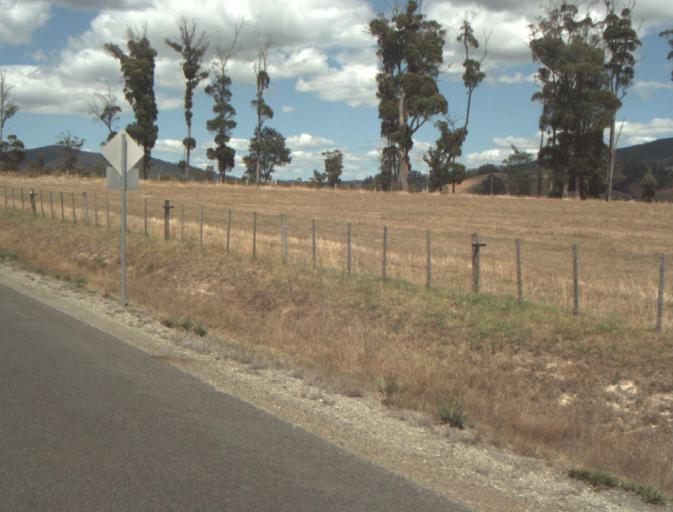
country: AU
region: Tasmania
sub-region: Launceston
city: Mayfield
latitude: -41.2280
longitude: 147.1440
